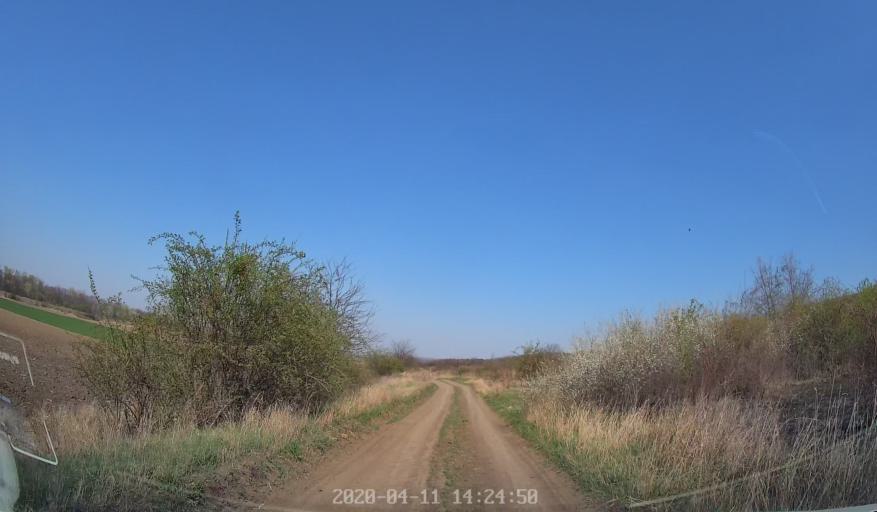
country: MD
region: Chisinau
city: Vadul lui Voda
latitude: 47.0924
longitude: 29.1438
